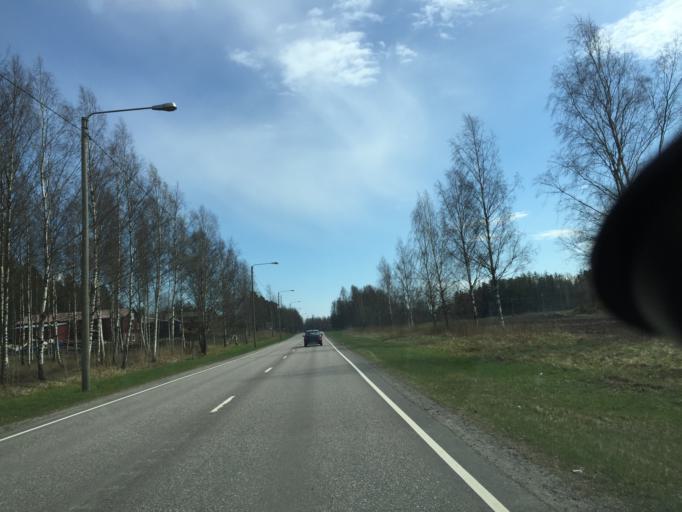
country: FI
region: Uusimaa
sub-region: Raaseporin
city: Ekenaes
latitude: 59.9951
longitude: 23.4084
